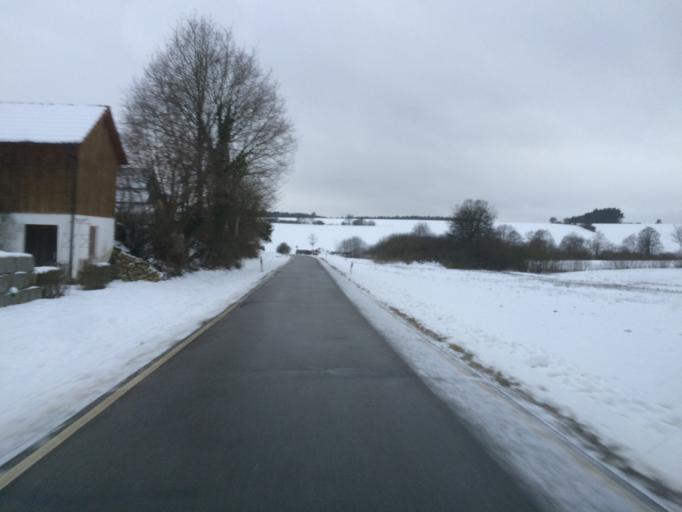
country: DE
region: Bavaria
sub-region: Upper Palatinate
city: Breitenbrunn
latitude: 49.3717
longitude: 12.0233
